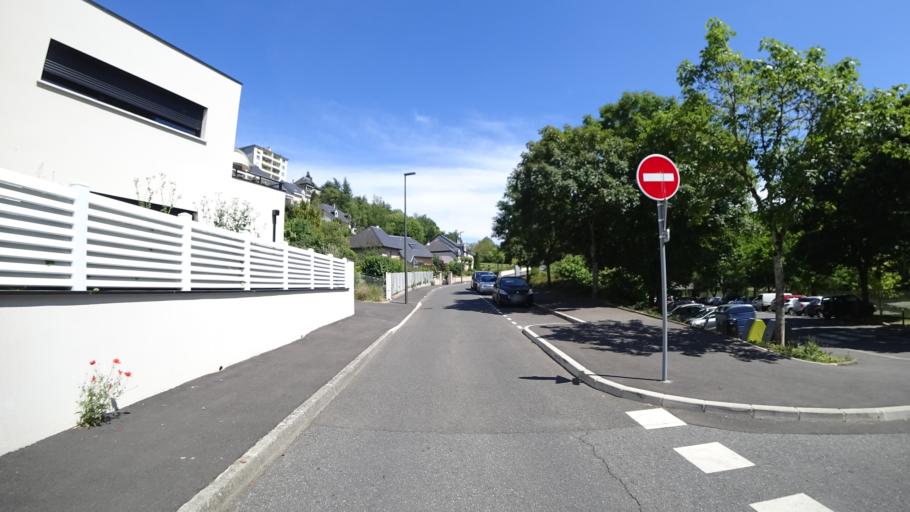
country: FR
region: Midi-Pyrenees
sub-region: Departement de l'Aveyron
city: Rodez
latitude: 44.3540
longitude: 2.5854
